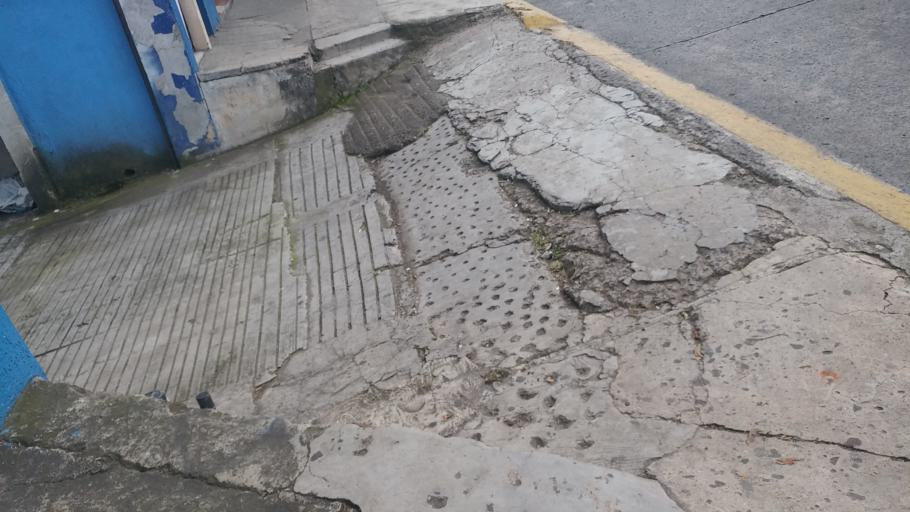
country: MX
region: Veracruz
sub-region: Xalapa
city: Xalapa de Enriquez
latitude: 19.5261
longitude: -96.9087
